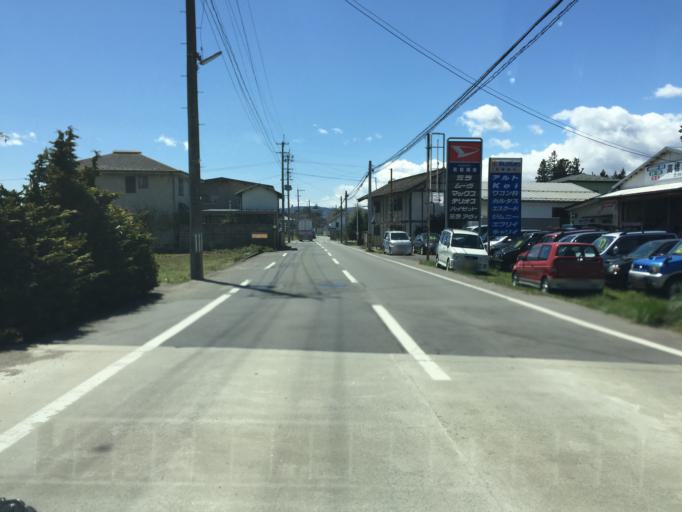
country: JP
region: Fukushima
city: Fukushima-shi
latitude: 37.7825
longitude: 140.4093
